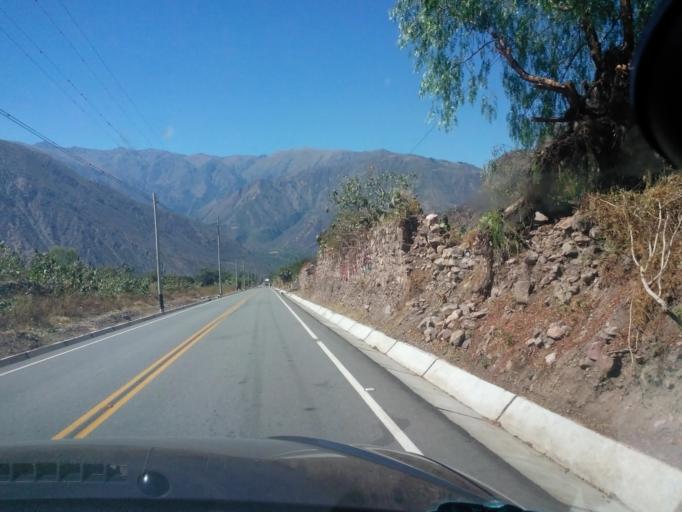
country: PE
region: Ayacucho
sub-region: Provincia de Huamanga
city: Ocros
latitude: -13.4216
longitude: -73.8588
